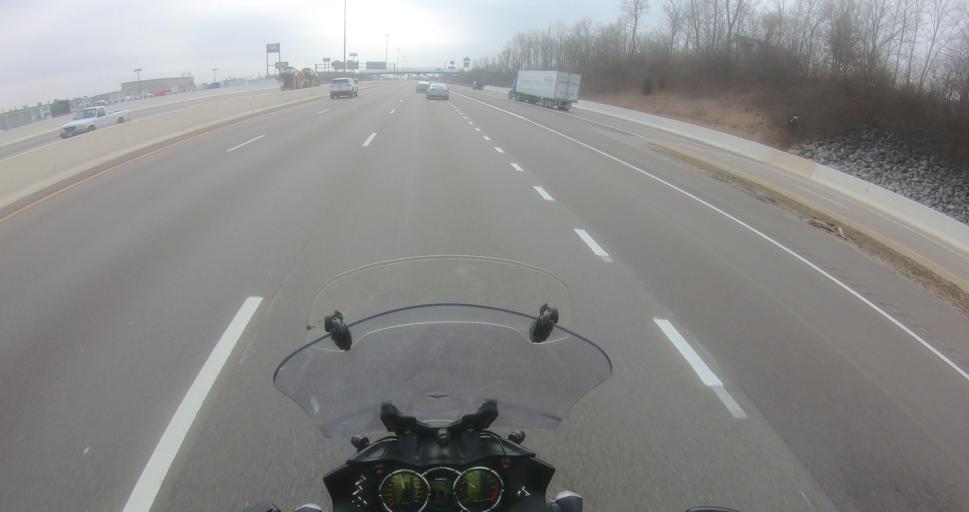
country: US
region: Ohio
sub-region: Montgomery County
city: Vandalia
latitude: 39.8600
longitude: -84.1897
